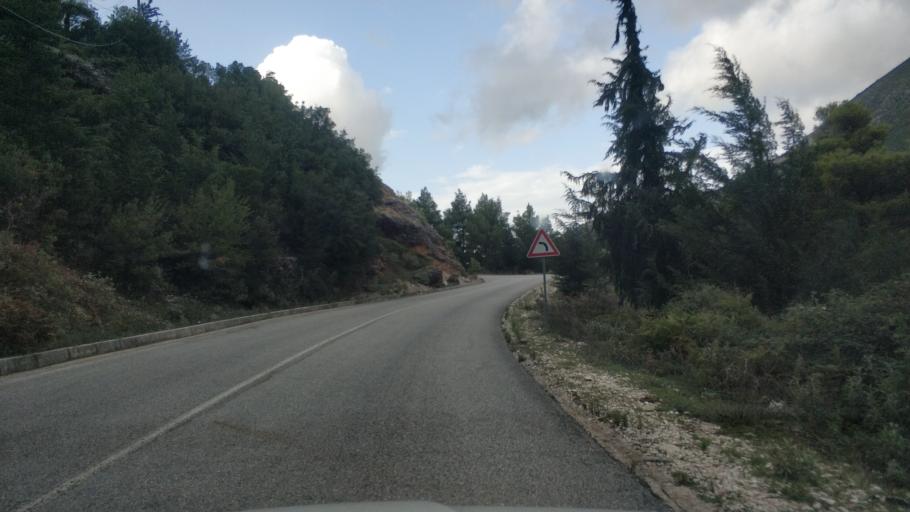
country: AL
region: Vlore
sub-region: Rrethi i Vlores
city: Orikum
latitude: 40.2500
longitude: 19.5422
